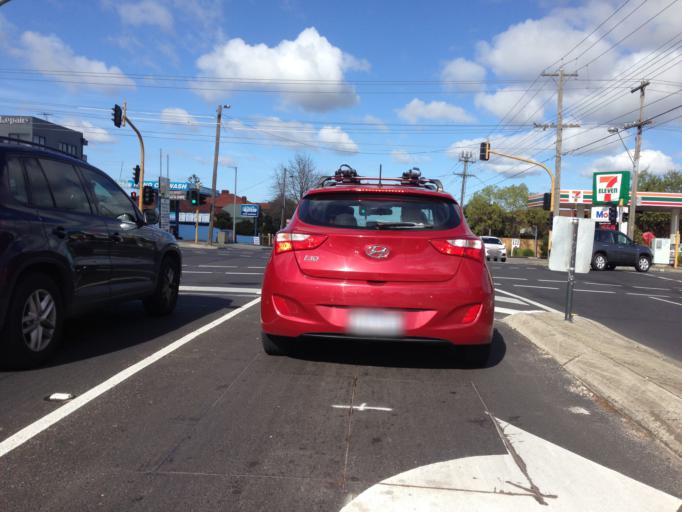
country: AU
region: Victoria
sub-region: Darebin
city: Fairfield
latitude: -37.7650
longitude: 145.0205
